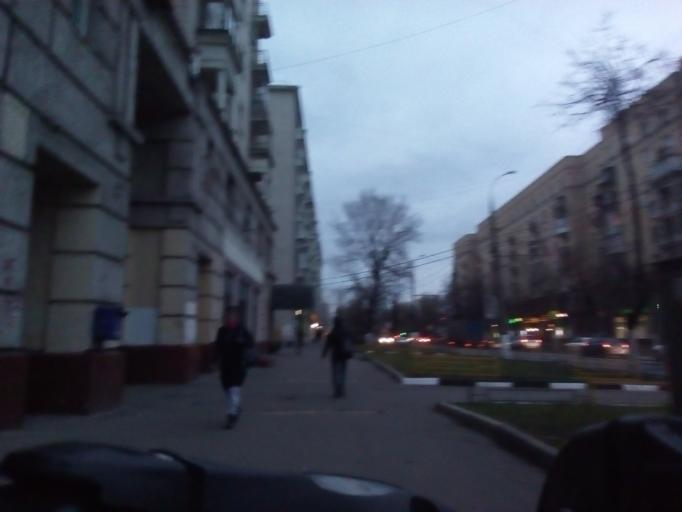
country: RU
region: Moscow
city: Lefortovo
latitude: 55.7452
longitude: 37.7219
